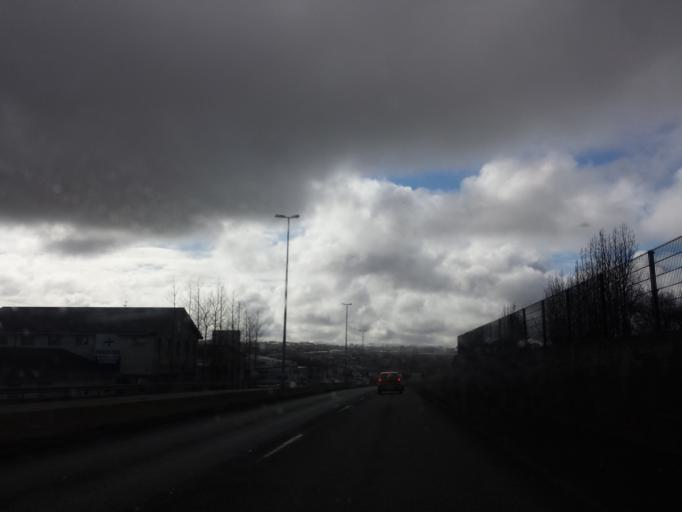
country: IS
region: Capital Region
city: Reykjavik
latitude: 64.1309
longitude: -21.8498
